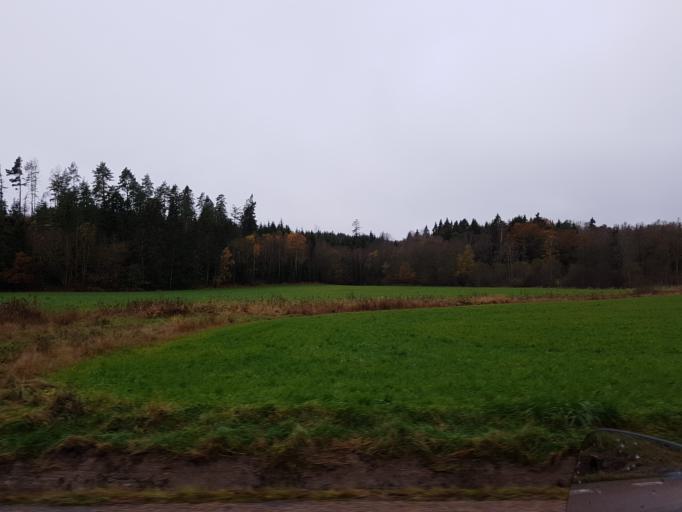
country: SE
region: Vaestra Goetaland
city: Svanesund
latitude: 58.2000
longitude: 11.8254
